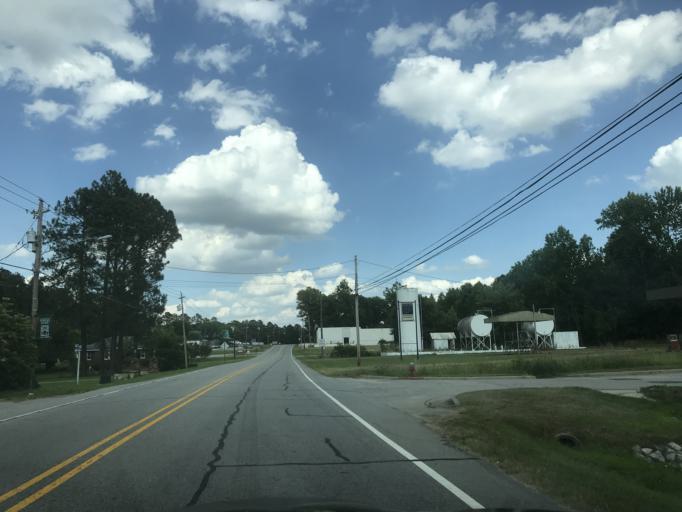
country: US
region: North Carolina
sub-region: Nash County
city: Spring Hope
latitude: 35.9515
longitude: -78.1027
